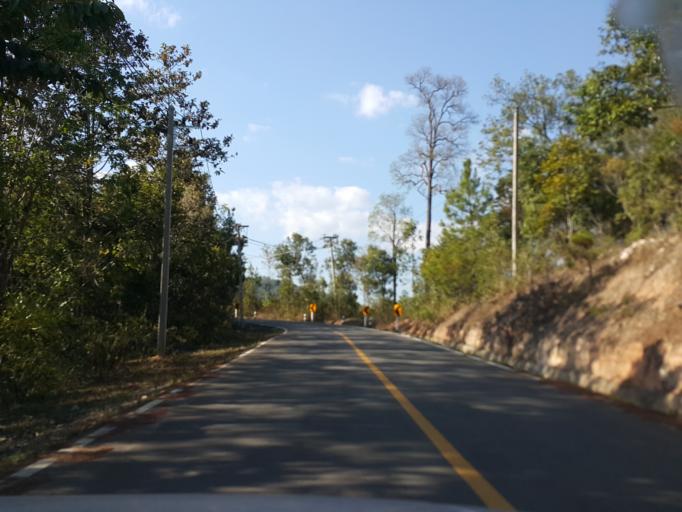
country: TH
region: Chiang Mai
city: Mae Wang
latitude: 18.6840
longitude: 98.5613
